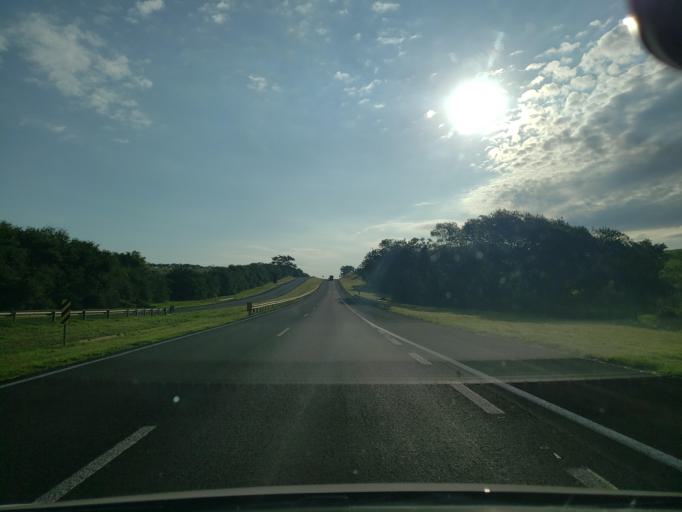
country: BR
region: Sao Paulo
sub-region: Valparaiso
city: Valparaiso
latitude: -21.2066
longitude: -50.8826
